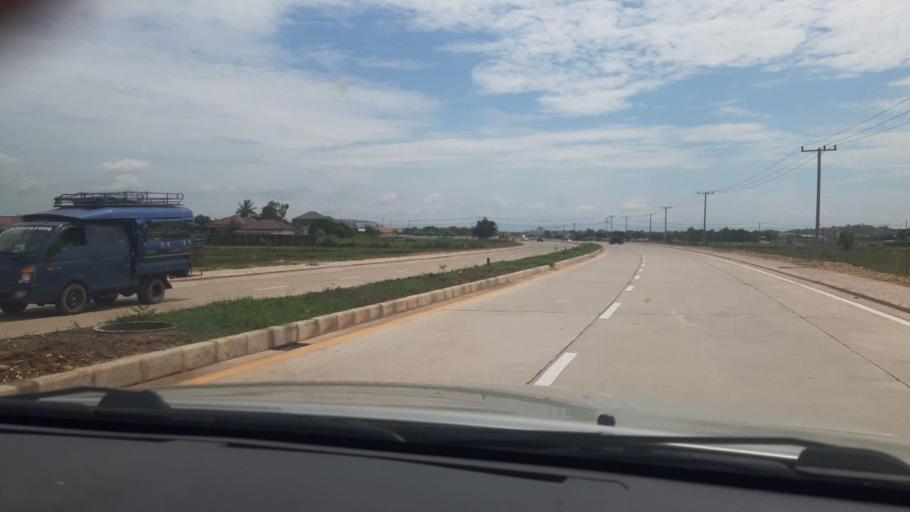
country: LA
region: Vientiane
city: Vientiane
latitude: 18.0292
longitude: 102.6073
